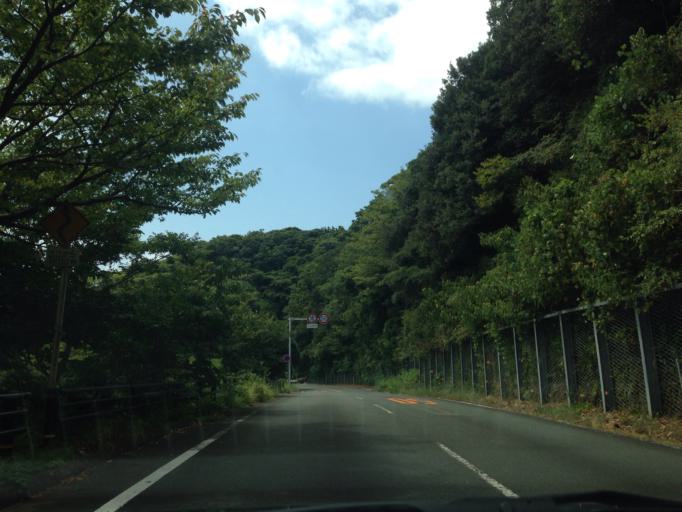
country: JP
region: Shizuoka
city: Shimoda
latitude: 34.6728
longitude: 138.7857
